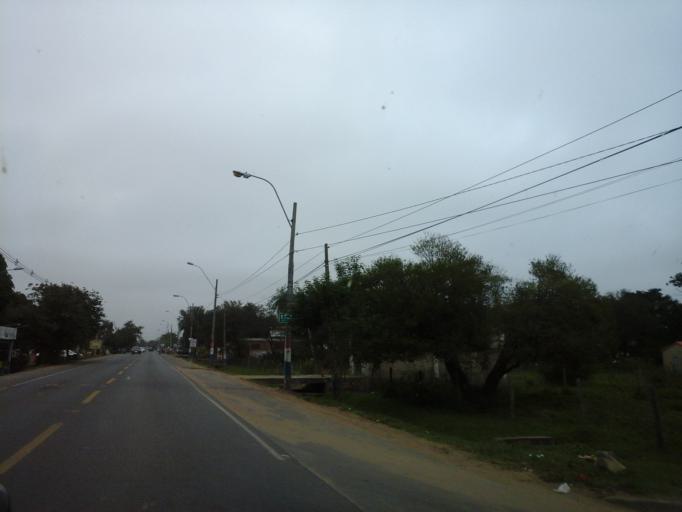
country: PY
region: Neembucu
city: Pilar
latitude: -26.8424
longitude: -58.2913
